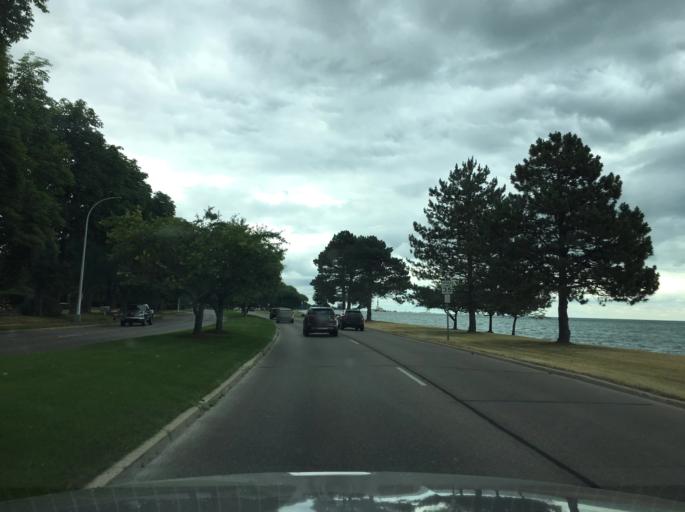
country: US
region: Michigan
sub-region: Wayne County
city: Grosse Pointe Farms
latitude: 42.4178
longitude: -82.8823
